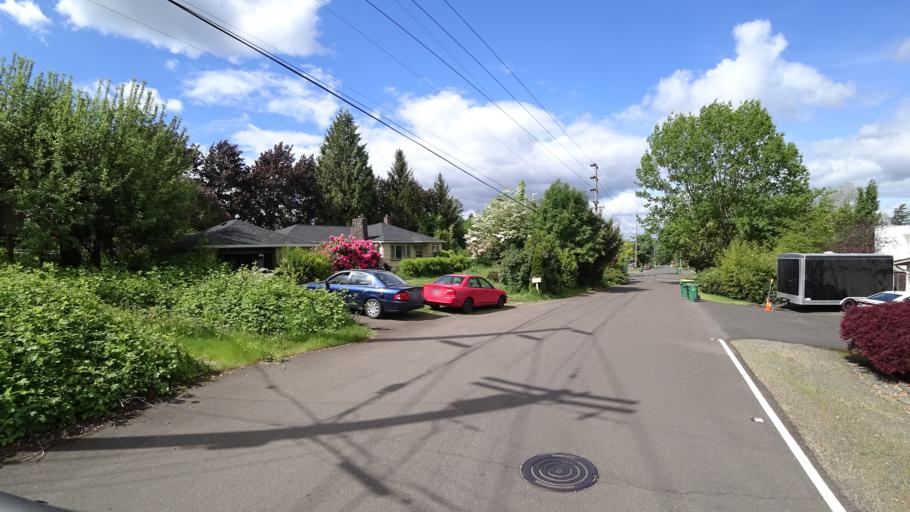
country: US
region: Oregon
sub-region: Washington County
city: Metzger
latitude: 45.4432
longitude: -122.7467
